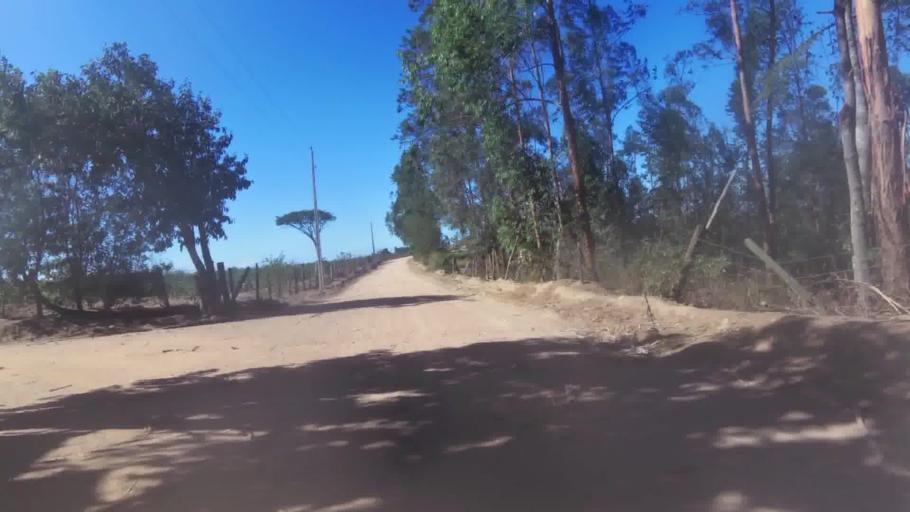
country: BR
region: Espirito Santo
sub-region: Marataizes
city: Marataizes
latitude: -21.1331
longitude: -40.9881
